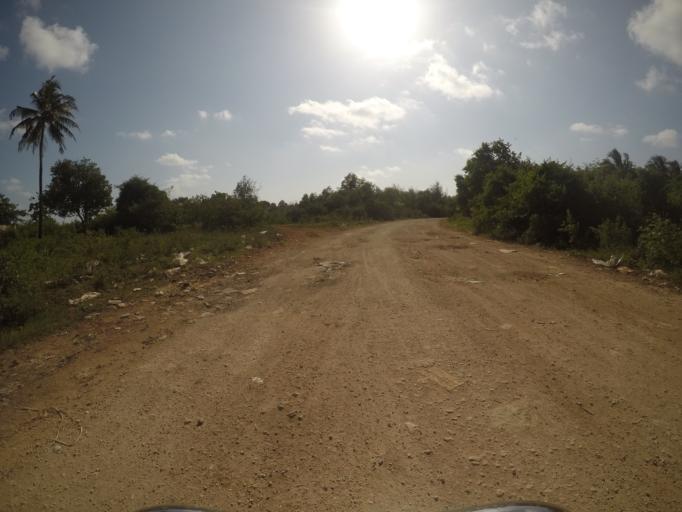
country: TZ
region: Zanzibar Central/South
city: Koani
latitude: -6.2190
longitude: 39.3279
